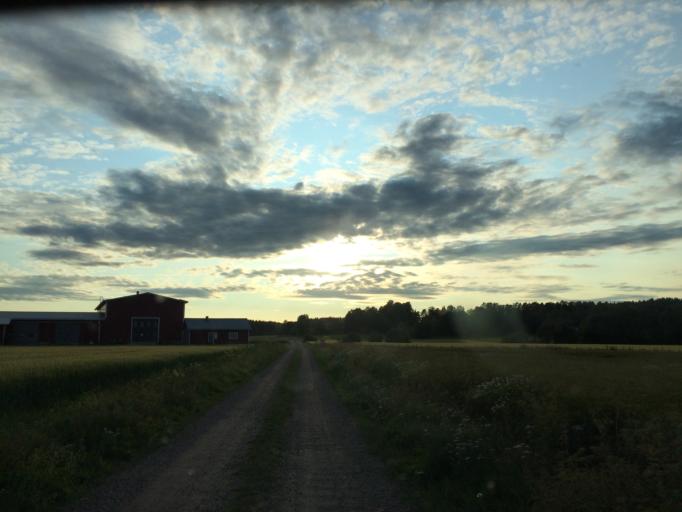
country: FI
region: Haeme
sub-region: Haemeenlinna
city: Turenki
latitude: 60.8859
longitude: 24.6296
